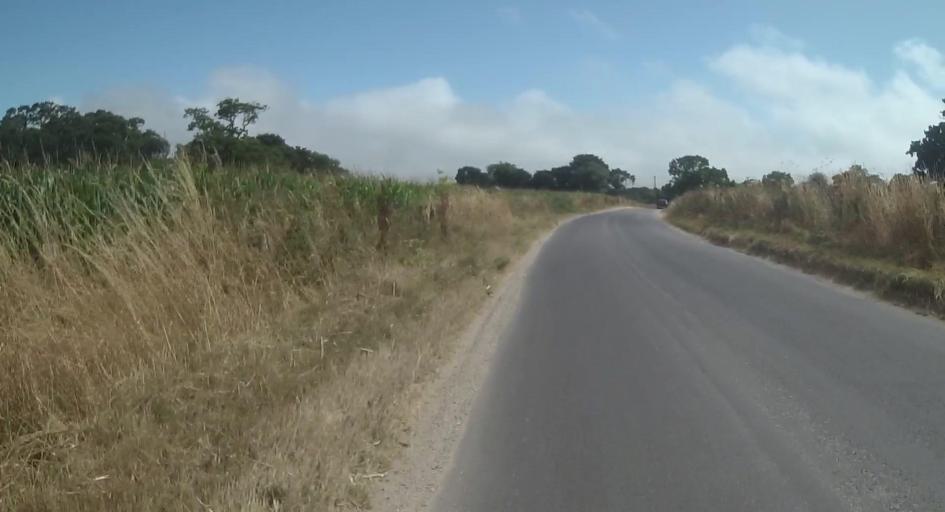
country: GB
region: England
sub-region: Dorset
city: Bovington Camp
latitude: 50.6960
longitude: -2.2708
